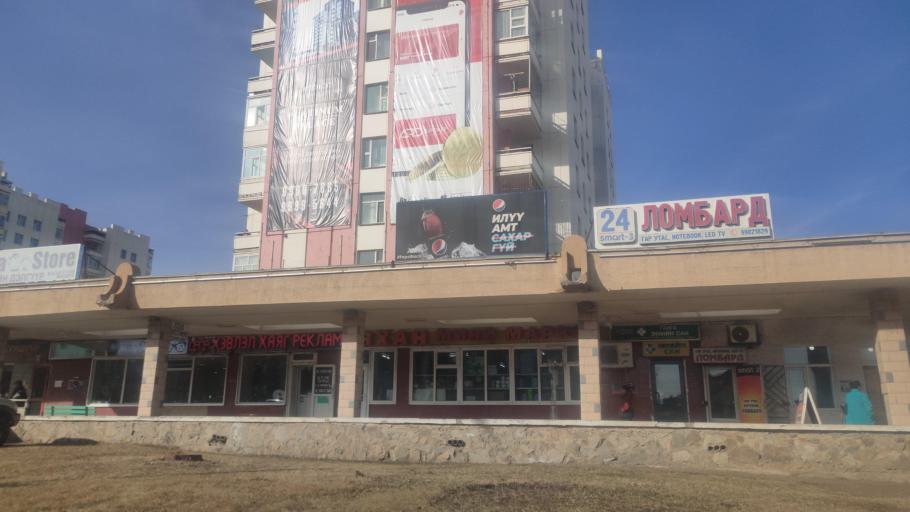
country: MN
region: Orhon
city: Erdenet
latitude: 49.0293
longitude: 104.0516
